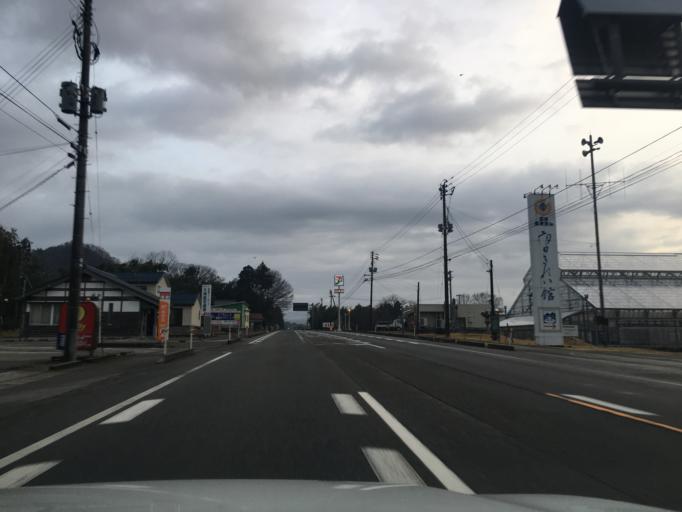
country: JP
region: Niigata
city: Murakami
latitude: 38.2834
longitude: 139.5224
